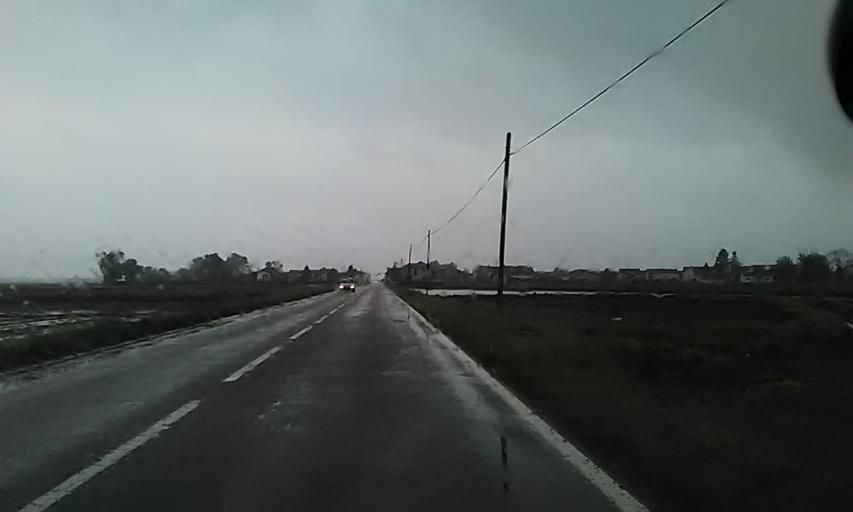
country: IT
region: Piedmont
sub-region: Provincia di Vercelli
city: Oldenico
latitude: 45.3979
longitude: 8.3792
